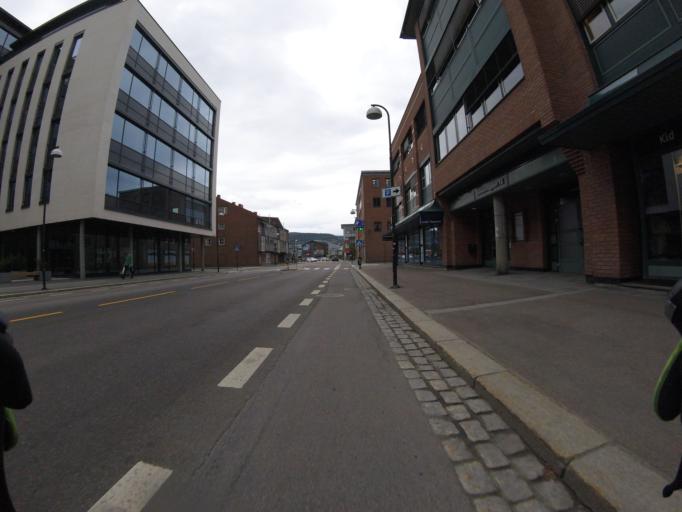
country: NO
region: Akershus
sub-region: Skedsmo
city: Lillestrom
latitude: 59.9571
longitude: 11.0511
